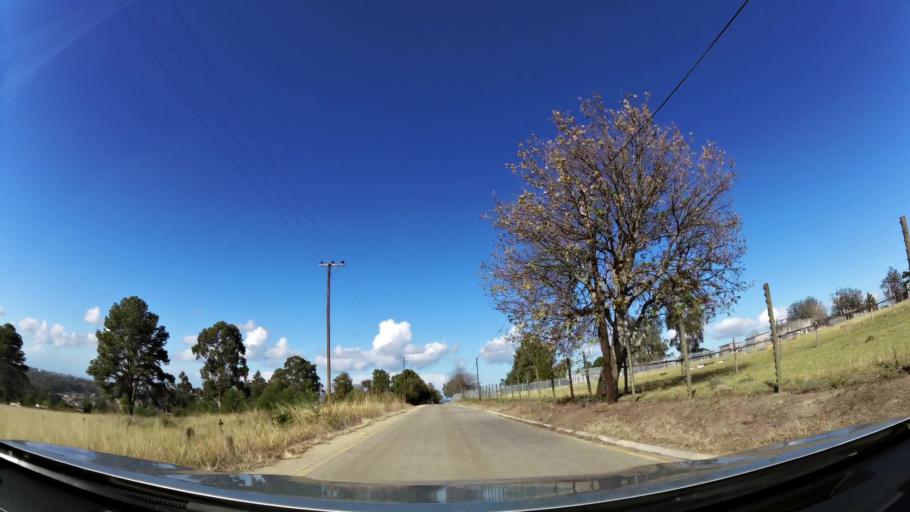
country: ZA
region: Western Cape
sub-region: Eden District Municipality
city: George
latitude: -33.9381
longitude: 22.4050
